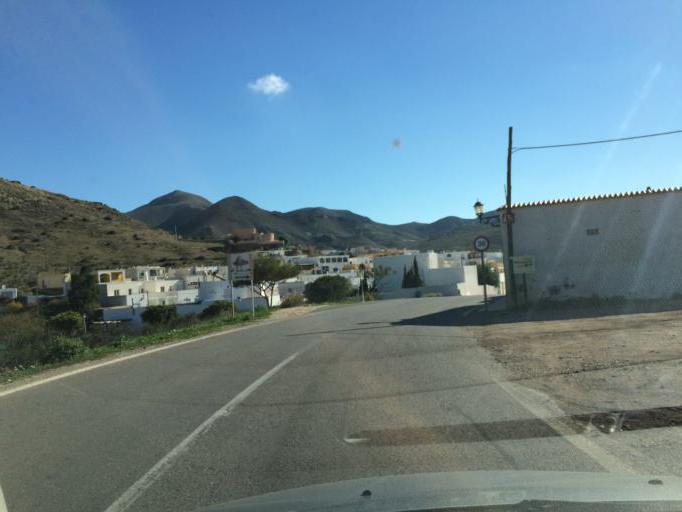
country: ES
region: Andalusia
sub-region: Provincia de Almeria
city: San Jose
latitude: 36.7901
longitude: -2.1107
